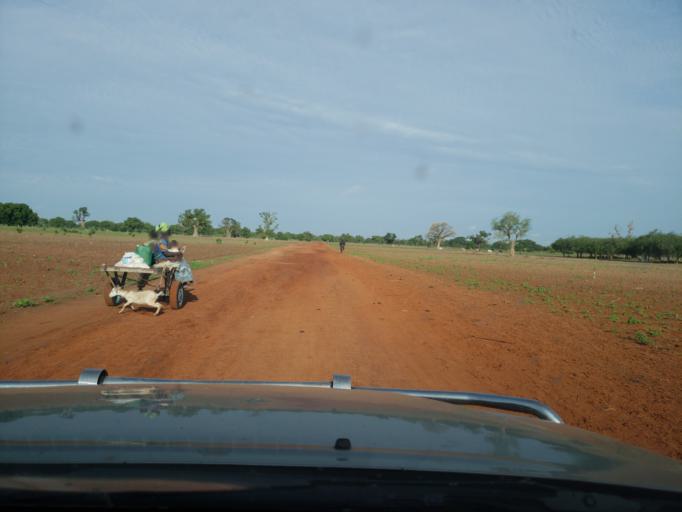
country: ML
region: Sikasso
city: Koutiala
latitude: 12.4213
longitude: -5.6916
